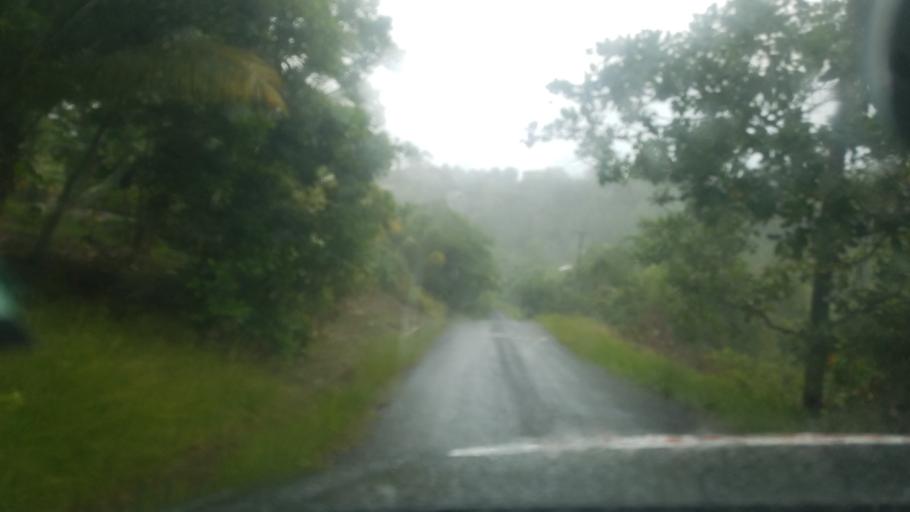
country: LC
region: Laborie Quarter
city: Laborie
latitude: 13.7656
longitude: -60.9729
